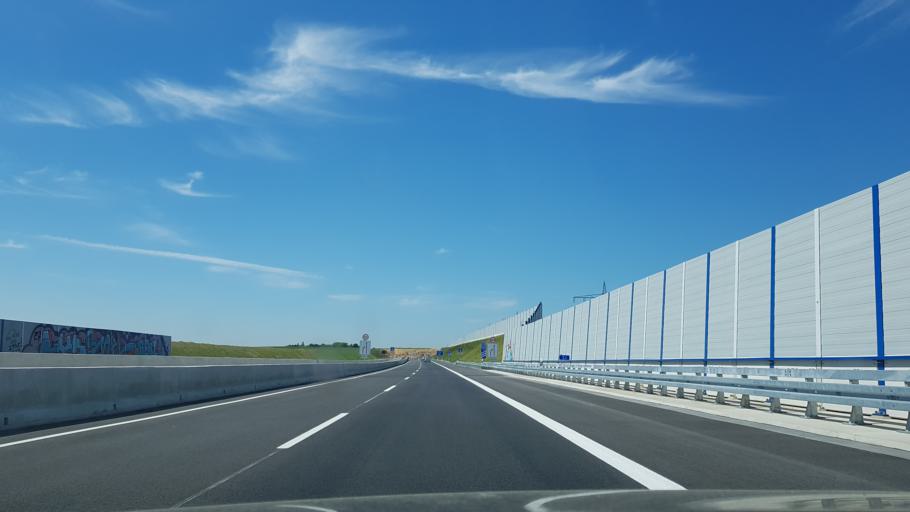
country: DE
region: North Rhine-Westphalia
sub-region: Regierungsbezirk Dusseldorf
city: Heiligenhaus
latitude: 51.3172
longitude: 6.9667
